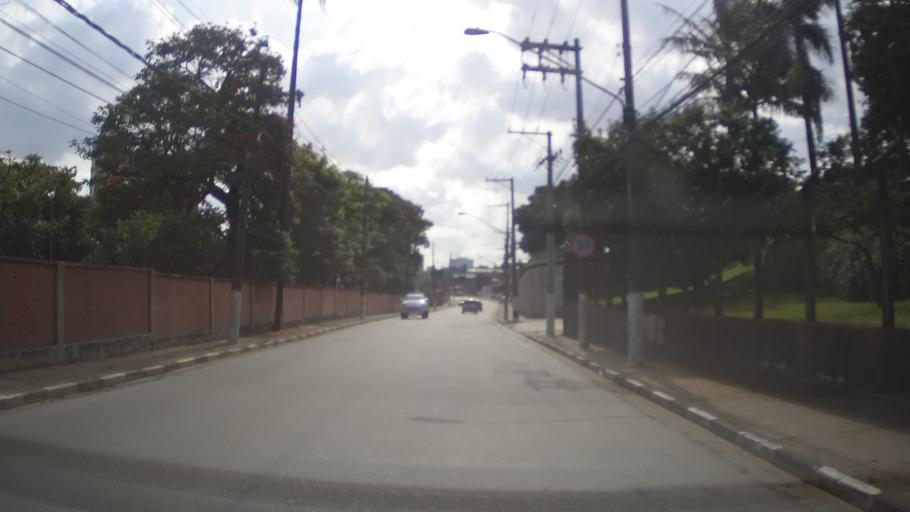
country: BR
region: Sao Paulo
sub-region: Guarulhos
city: Guarulhos
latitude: -23.4642
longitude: -46.5057
